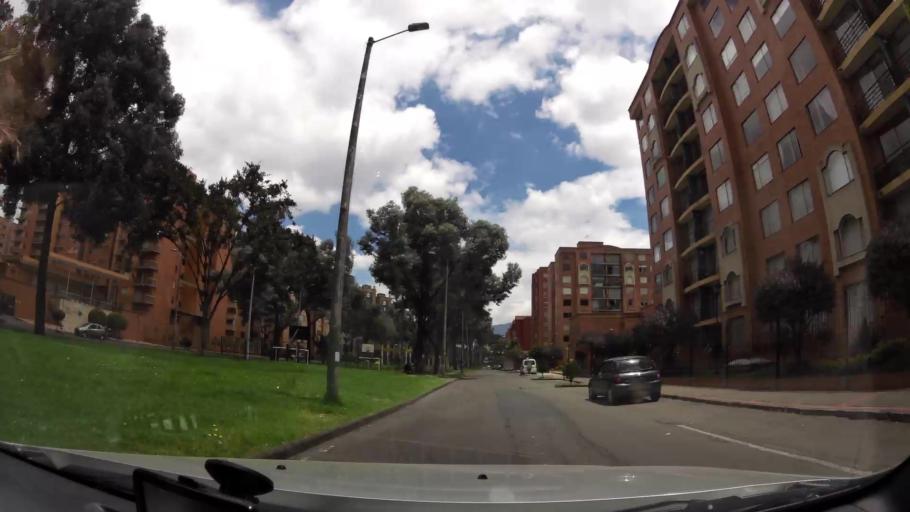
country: CO
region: Bogota D.C.
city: Bogota
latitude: 4.6424
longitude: -74.1032
